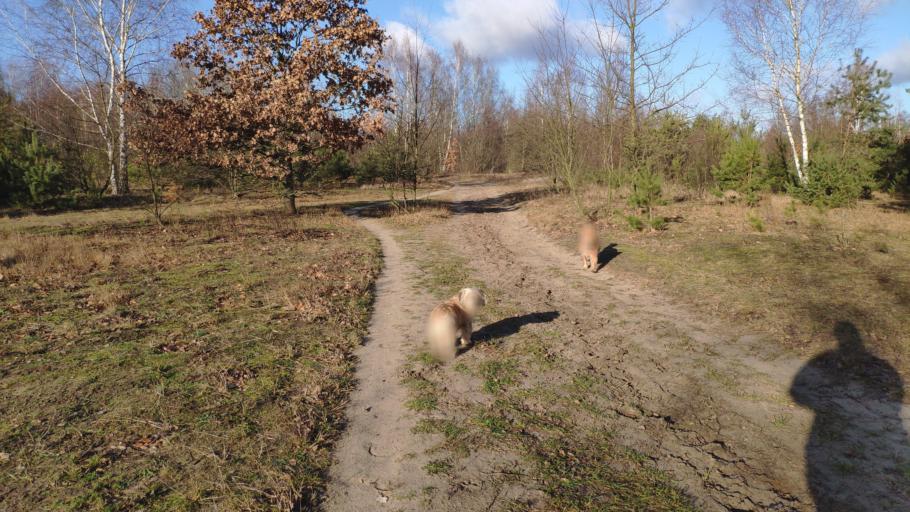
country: PL
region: Lodz Voivodeship
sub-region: Powiat pabianicki
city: Ksawerow
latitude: 51.7285
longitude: 19.4109
